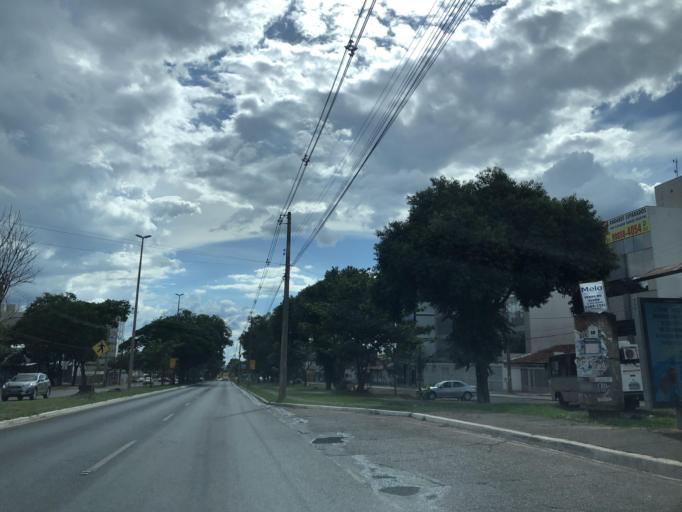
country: BR
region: Goias
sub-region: Luziania
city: Luziania
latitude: -16.0113
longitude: -48.0652
